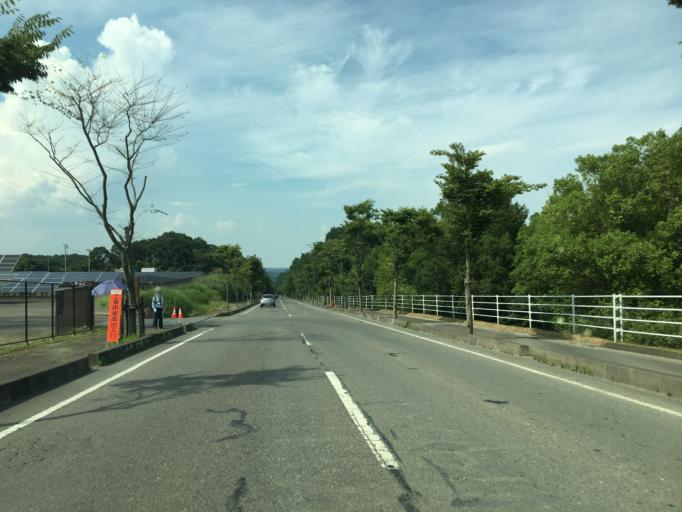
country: JP
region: Fukushima
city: Sukagawa
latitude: 37.2303
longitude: 140.4353
